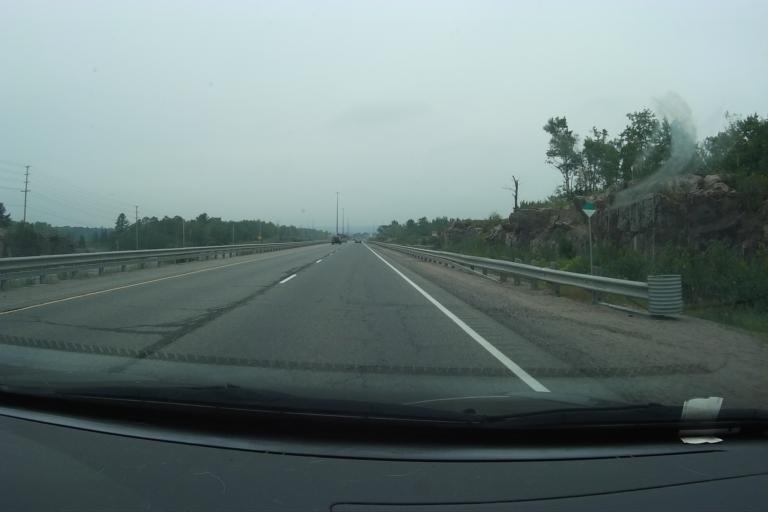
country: CA
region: Ontario
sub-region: Nipissing District
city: North Bay
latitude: 46.2975
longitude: -79.4259
